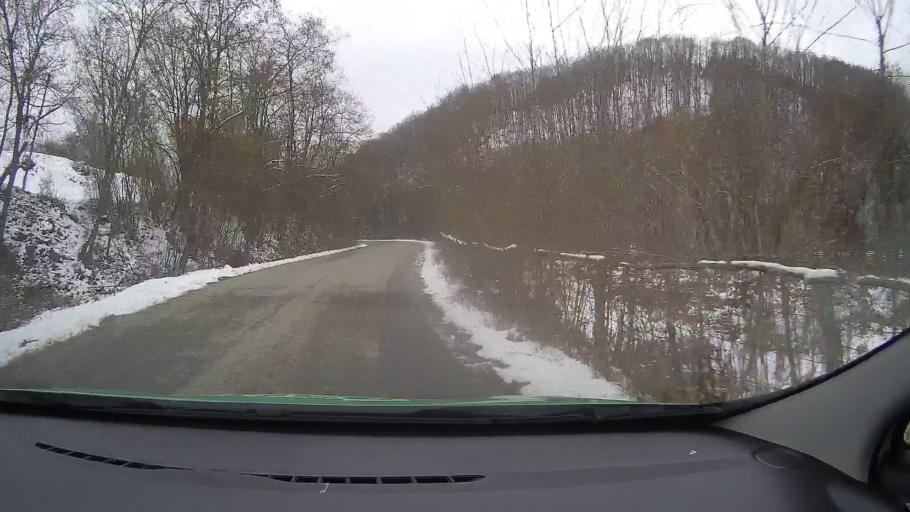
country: RO
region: Hunedoara
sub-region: Comuna Balsa
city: Balsa
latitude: 46.0436
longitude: 23.0711
